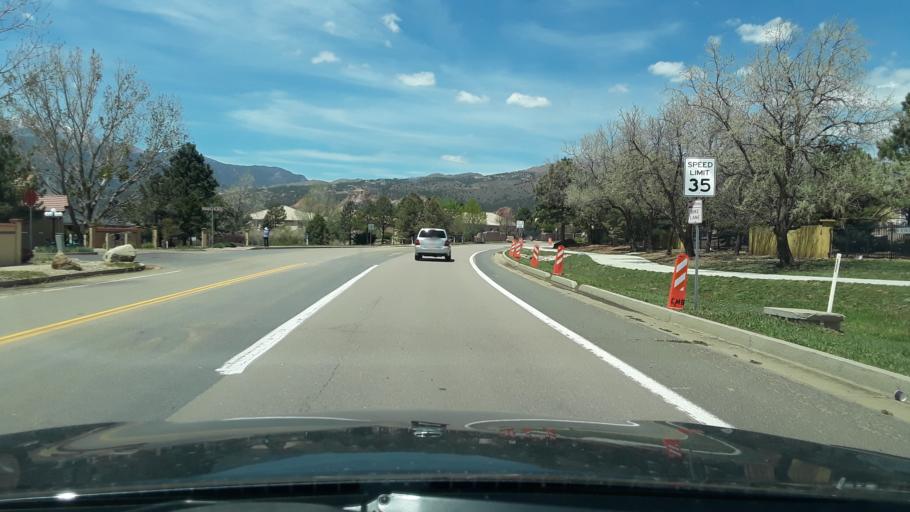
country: US
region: Colorado
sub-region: El Paso County
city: Colorado Springs
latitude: 38.8697
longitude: -104.8614
